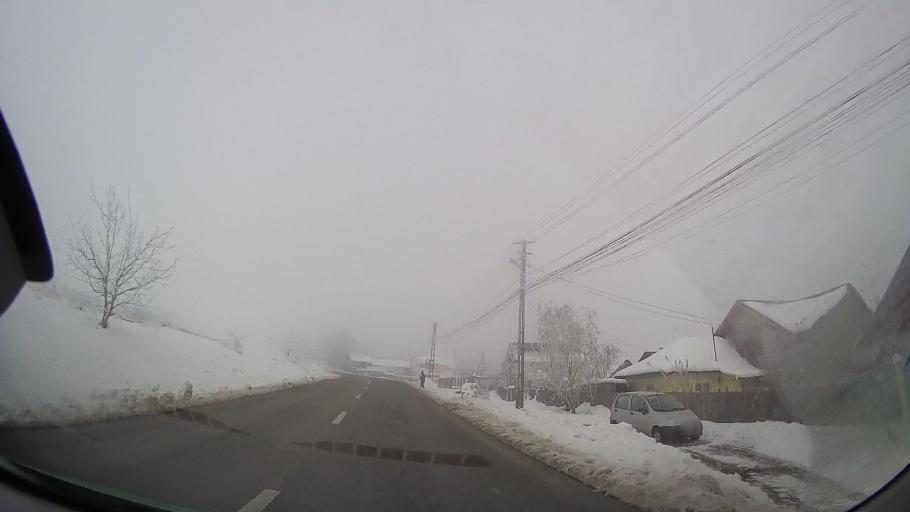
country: RO
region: Iasi
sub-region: Comuna Halaucesti
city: Halaucesti
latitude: 47.1014
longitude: 26.8160
